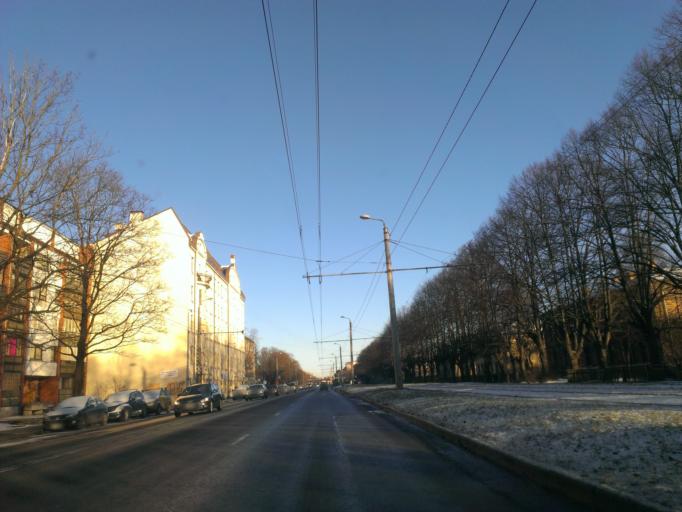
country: LV
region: Riga
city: Riga
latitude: 56.9727
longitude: 24.1103
